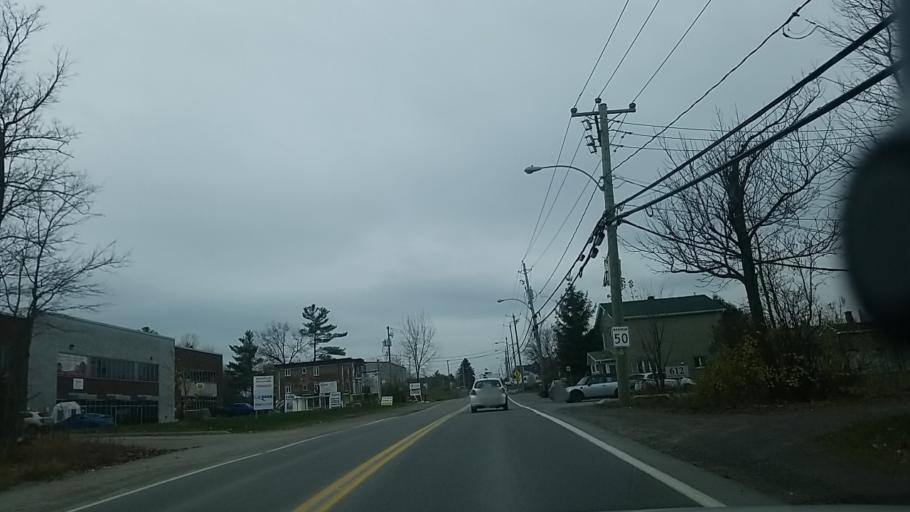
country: CA
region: Quebec
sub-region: Laurentides
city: Saint-Jerome
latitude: 45.7781
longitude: -74.0323
